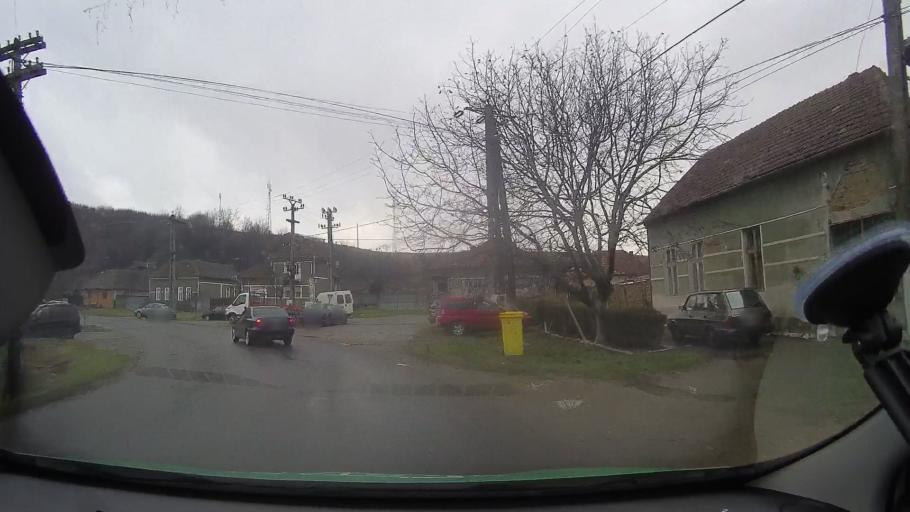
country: RO
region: Arad
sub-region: Comuna Sebis
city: Sebis
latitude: 46.3779
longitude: 22.1359
